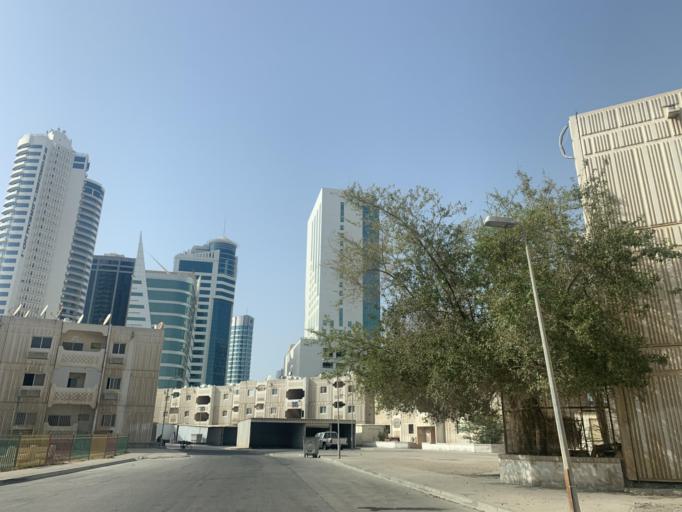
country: BH
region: Manama
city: Jidd Hafs
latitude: 26.2277
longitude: 50.5508
